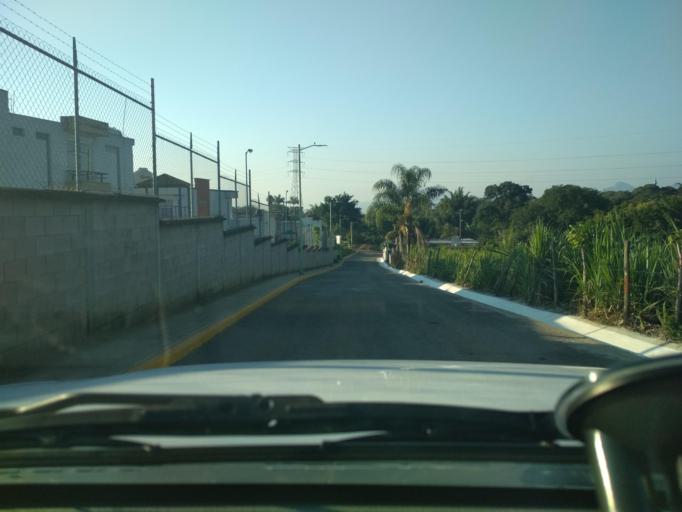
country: MX
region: Veracruz
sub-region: Fortin
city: Fraccionamiento Villas de la Llave
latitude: 18.9162
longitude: -96.9969
